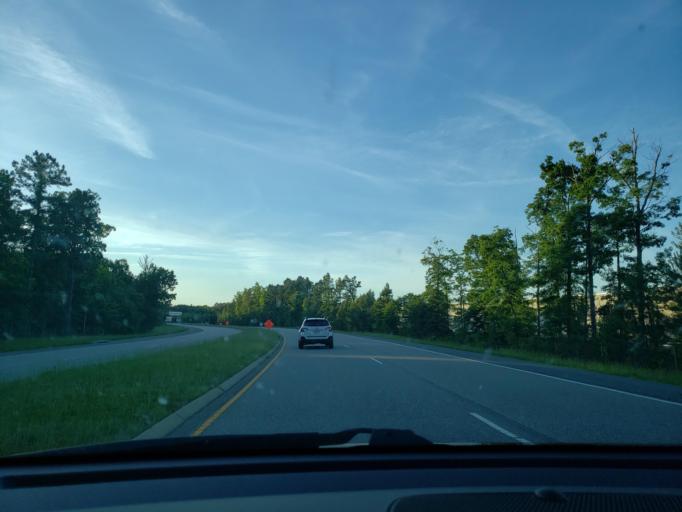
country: US
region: Virginia
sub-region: Henrico County
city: Fort Lee
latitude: 37.4821
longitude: -77.3404
